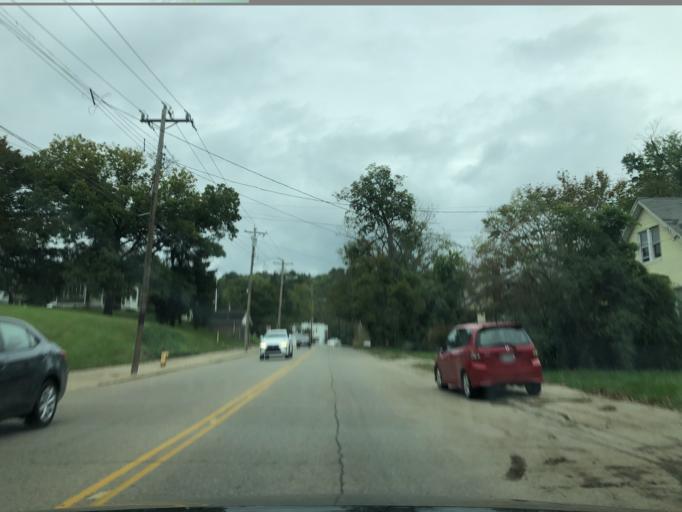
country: US
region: Ohio
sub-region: Hamilton County
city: Mariemont
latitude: 39.1582
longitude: -84.3813
